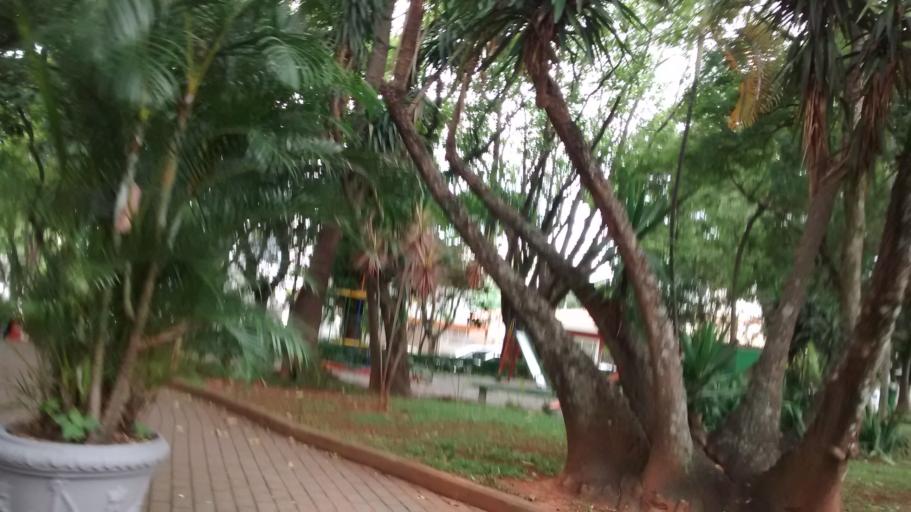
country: BR
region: Sao Paulo
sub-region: Sao Paulo
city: Sao Paulo
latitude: -23.5765
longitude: -46.7119
